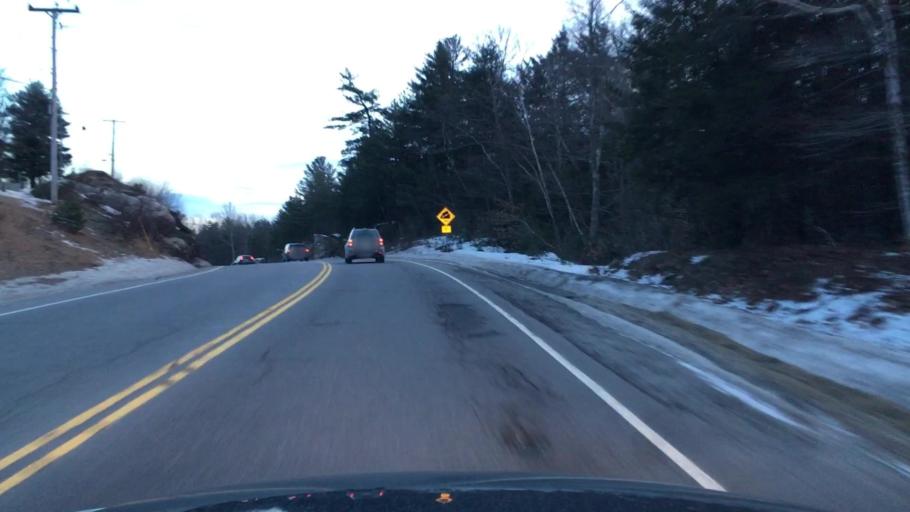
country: US
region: New Hampshire
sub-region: Merrimack County
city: Newbury
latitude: 43.3158
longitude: -72.0328
